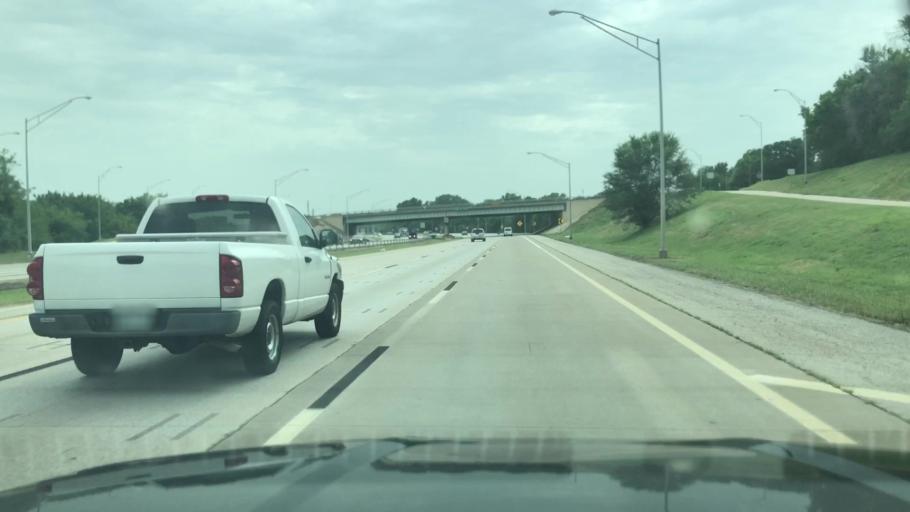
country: US
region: Oklahoma
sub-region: Tulsa County
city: Sand Springs
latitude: 36.1532
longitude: -96.0632
